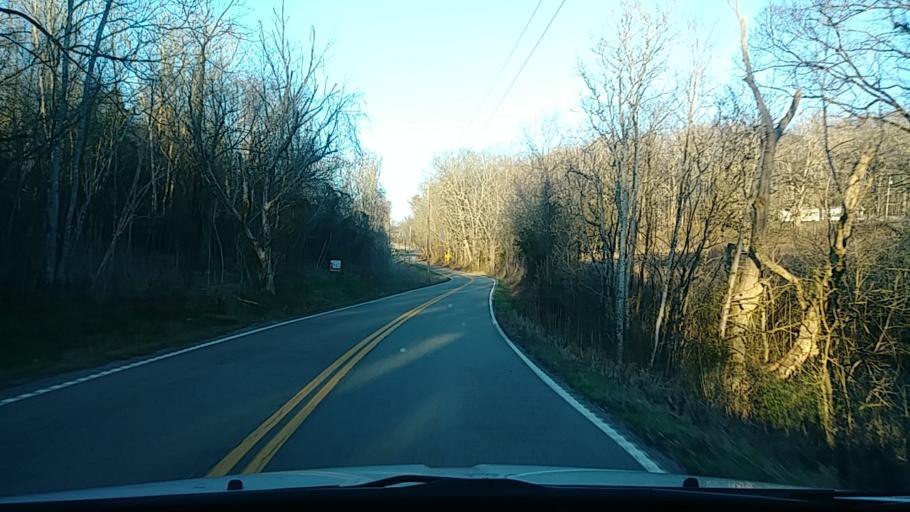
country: US
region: Tennessee
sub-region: Jefferson County
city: White Pine
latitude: 36.1240
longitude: -83.1178
